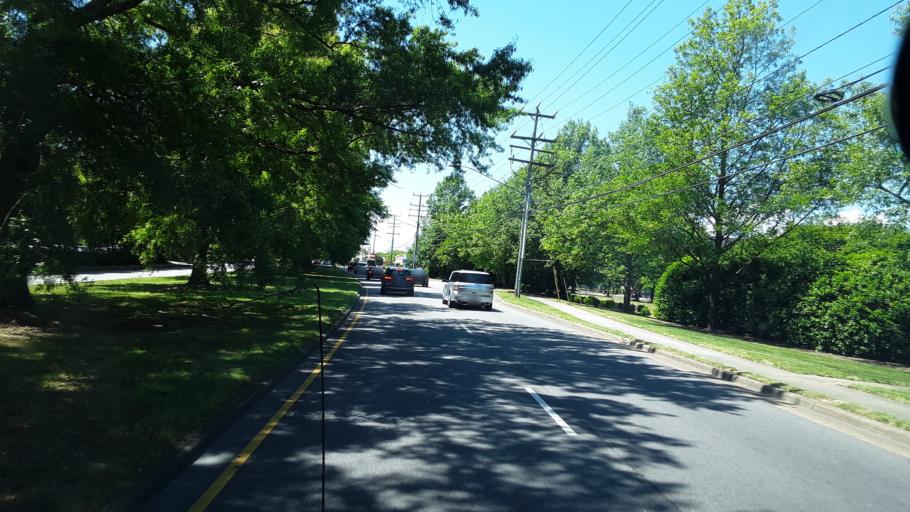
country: US
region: Virginia
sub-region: City of Virginia Beach
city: Virginia Beach
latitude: 36.7712
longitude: -76.0117
